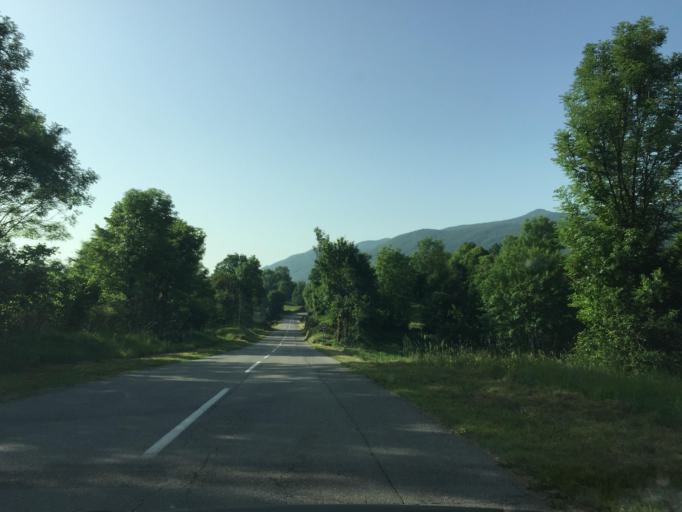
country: HR
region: Primorsko-Goranska
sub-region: Grad Opatija
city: Opatija
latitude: 45.4376
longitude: 14.1983
